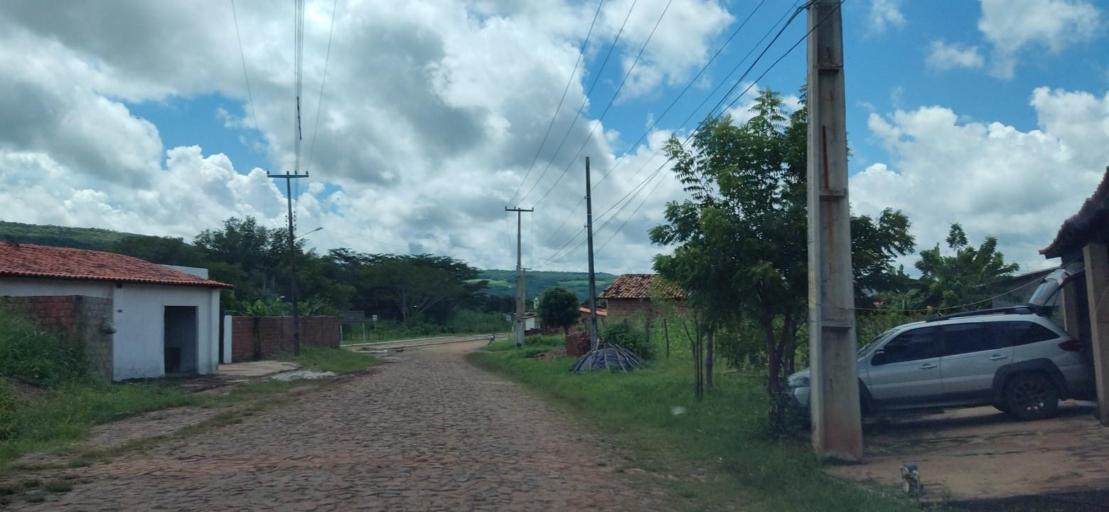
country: BR
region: Piaui
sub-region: Valenca Do Piaui
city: Valenca do Piaui
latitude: -6.1114
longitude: -41.7972
